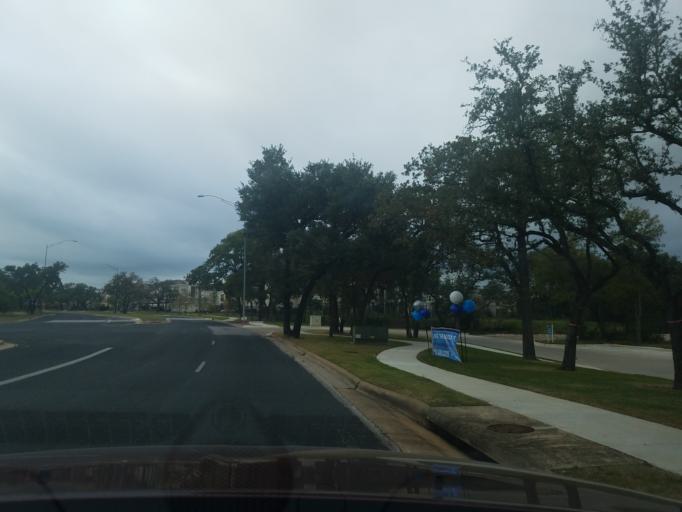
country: US
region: Texas
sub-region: Williamson County
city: Anderson Mill
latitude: 30.4718
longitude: -97.8113
